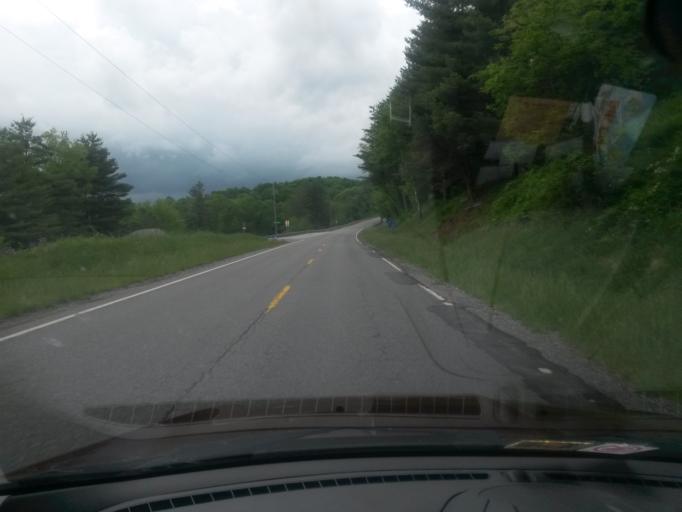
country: US
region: Virginia
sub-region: Floyd County
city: Floyd
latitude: 36.9403
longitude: -80.3468
